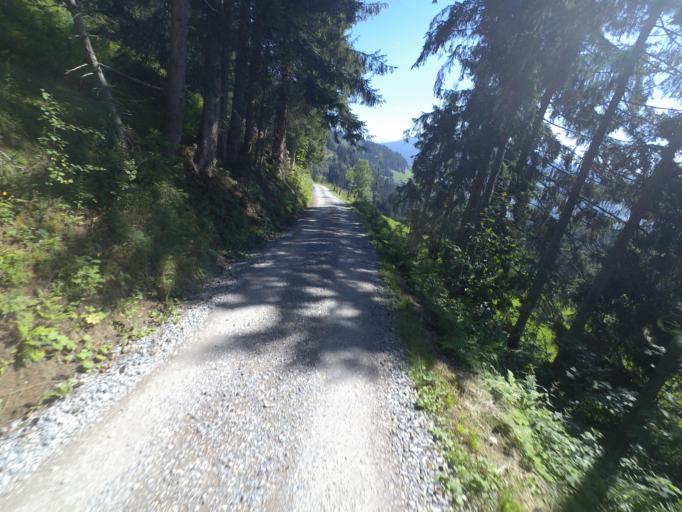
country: AT
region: Salzburg
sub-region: Politischer Bezirk Sankt Johann im Pongau
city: Sankt Veit im Pongau
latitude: 47.3604
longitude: 13.1683
